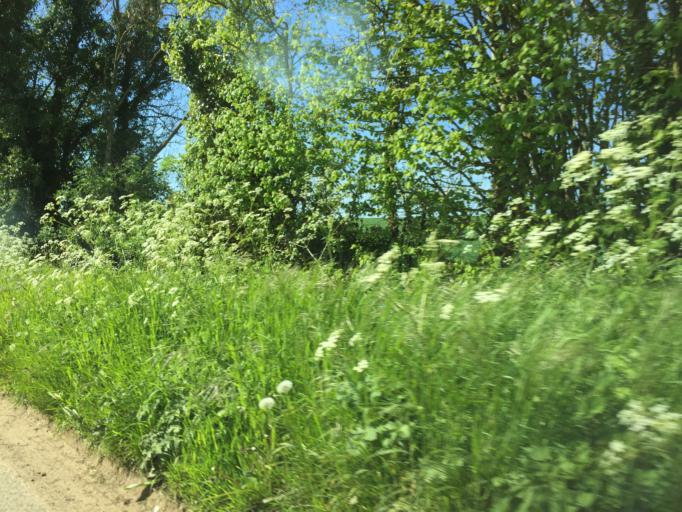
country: GB
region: England
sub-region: Wiltshire
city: Luckington
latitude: 51.5940
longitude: -2.2552
